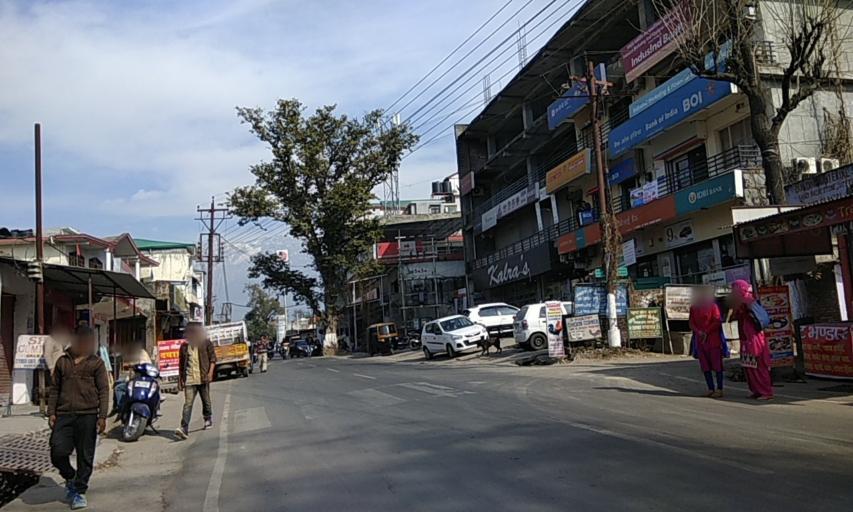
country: IN
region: Himachal Pradesh
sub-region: Kangra
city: Kangra
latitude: 32.1135
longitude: 76.2808
